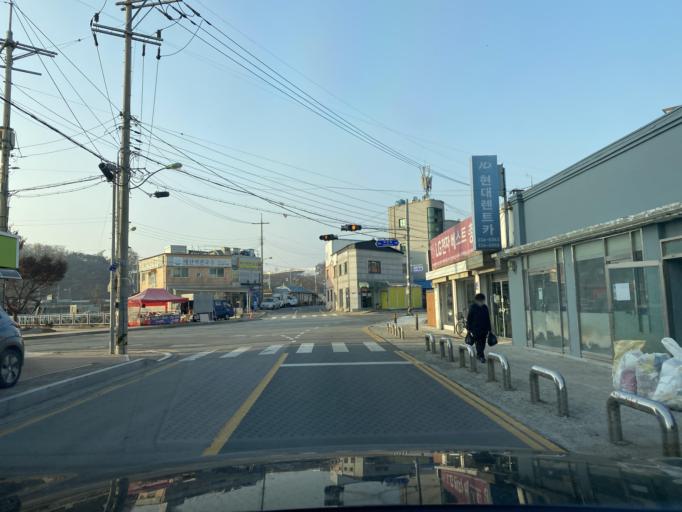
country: KR
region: Chungcheongnam-do
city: Yesan
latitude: 36.6888
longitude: 126.8301
